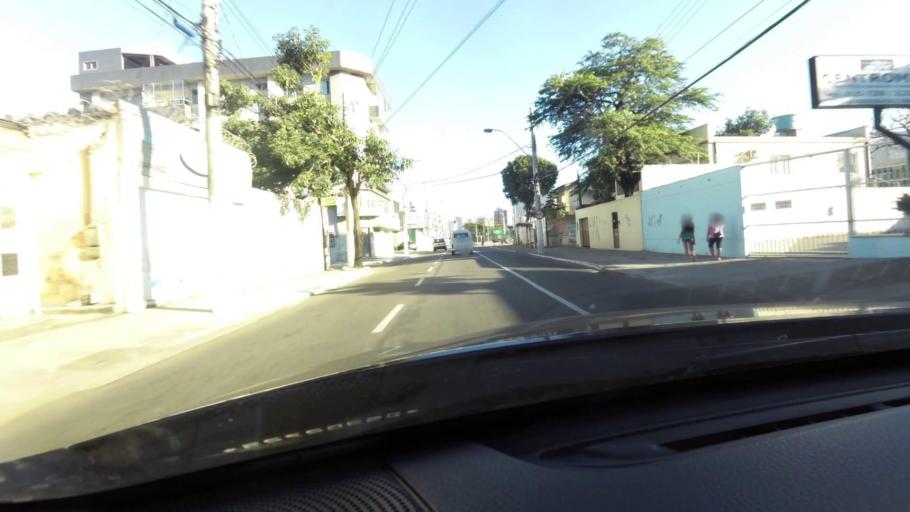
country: BR
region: Espirito Santo
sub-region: Vila Velha
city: Vila Velha
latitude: -20.3509
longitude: -40.2954
